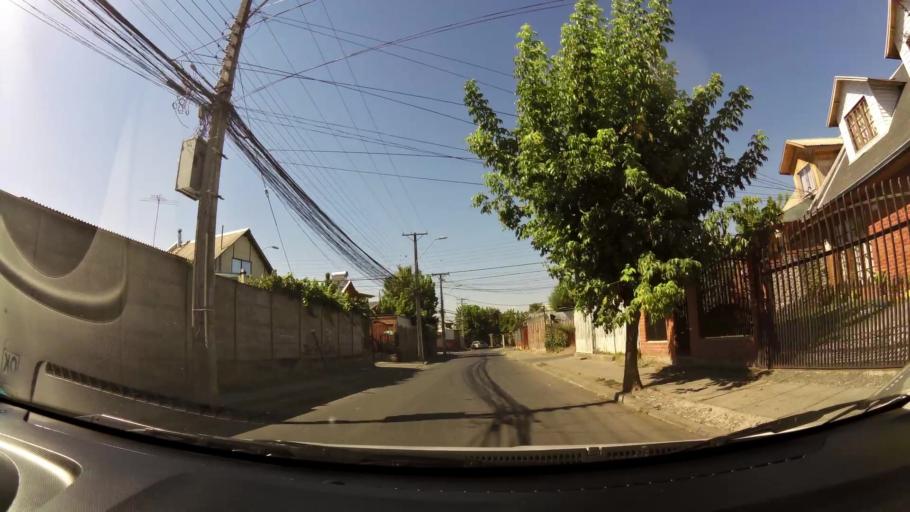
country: CL
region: Maule
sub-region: Provincia de Curico
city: Curico
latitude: -34.9775
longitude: -71.2600
